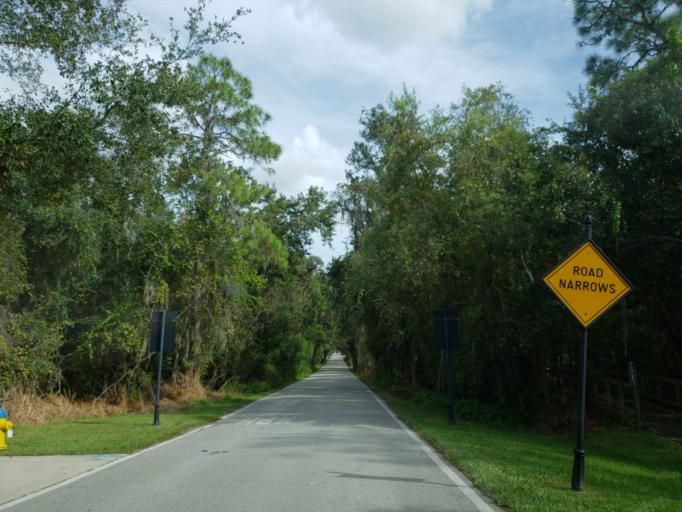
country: US
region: Florida
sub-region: Hillsborough County
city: Fish Hawk
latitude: 27.8428
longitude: -82.2276
